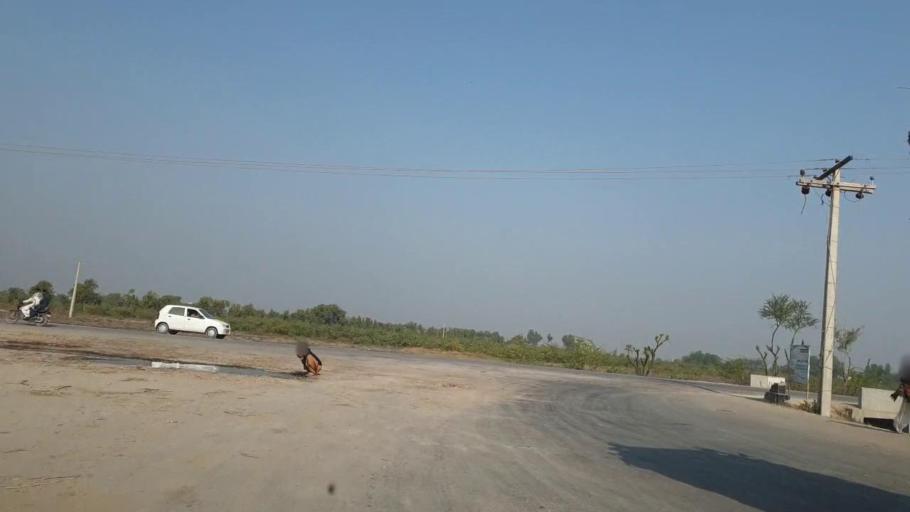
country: PK
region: Sindh
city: Mirpur Khas
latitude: 25.5472
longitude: 69.0443
